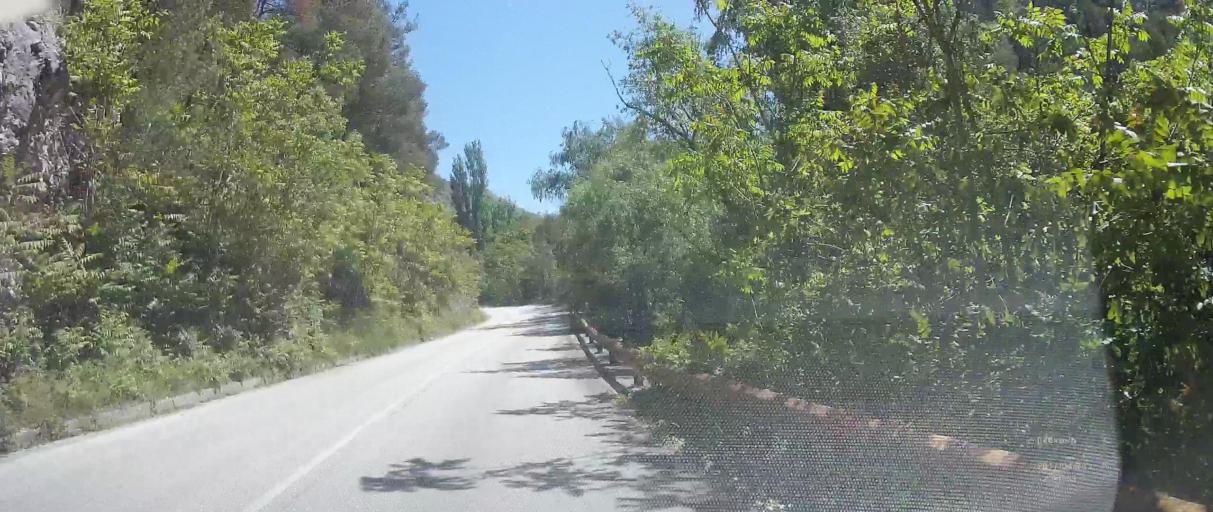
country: HR
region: Splitsko-Dalmatinska
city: Zrnovnica
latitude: 43.5209
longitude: 16.5655
